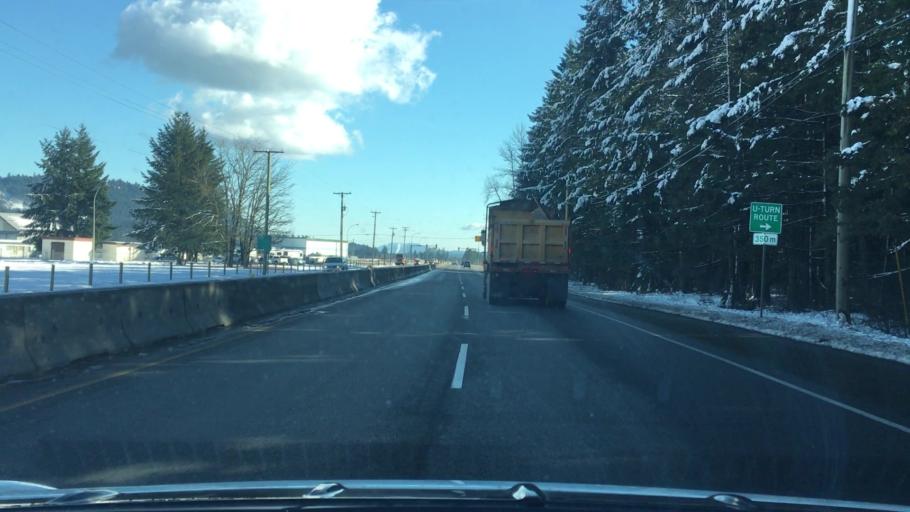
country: CA
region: British Columbia
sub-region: Cowichan Valley Regional District
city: Ladysmith
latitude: 49.0482
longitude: -123.8766
